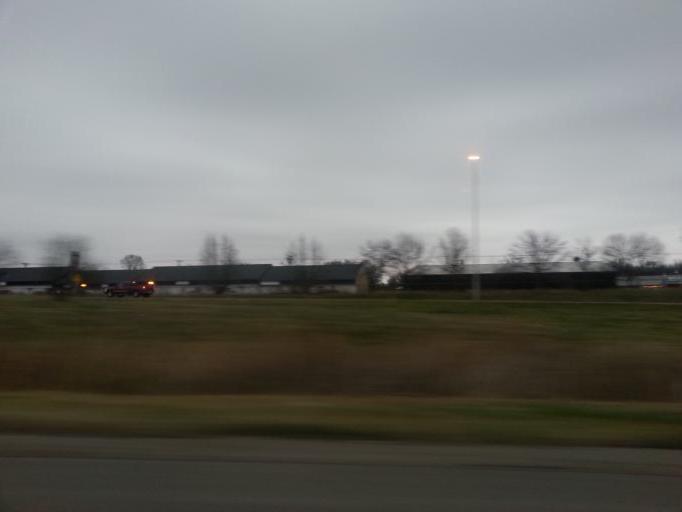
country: US
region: Iowa
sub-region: Linn County
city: Hiawatha
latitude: 42.0439
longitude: -91.6818
